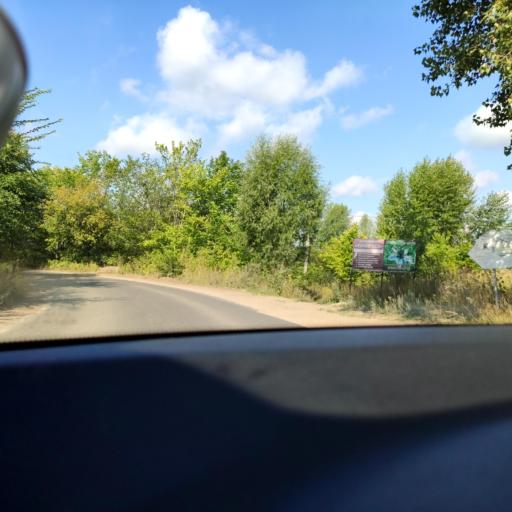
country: RU
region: Samara
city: Volzhskiy
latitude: 53.4340
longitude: 50.0926
